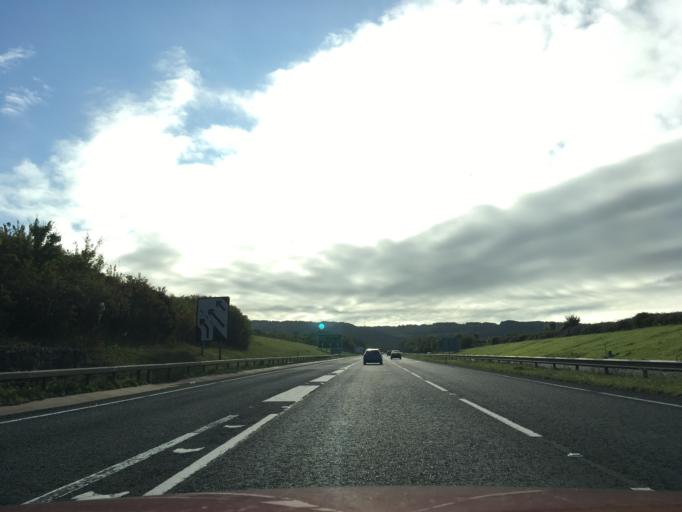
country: GB
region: England
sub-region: Gloucestershire
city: Churchdown
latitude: 51.8544
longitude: -2.1551
